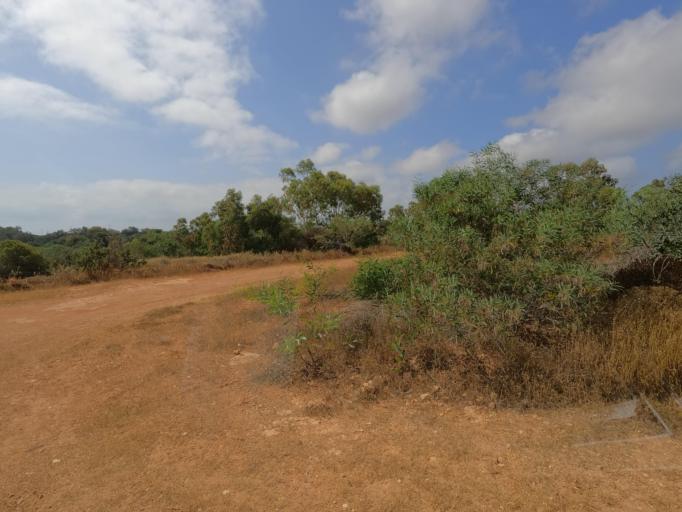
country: CY
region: Ammochostos
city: Protaras
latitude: 35.0057
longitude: 34.0428
